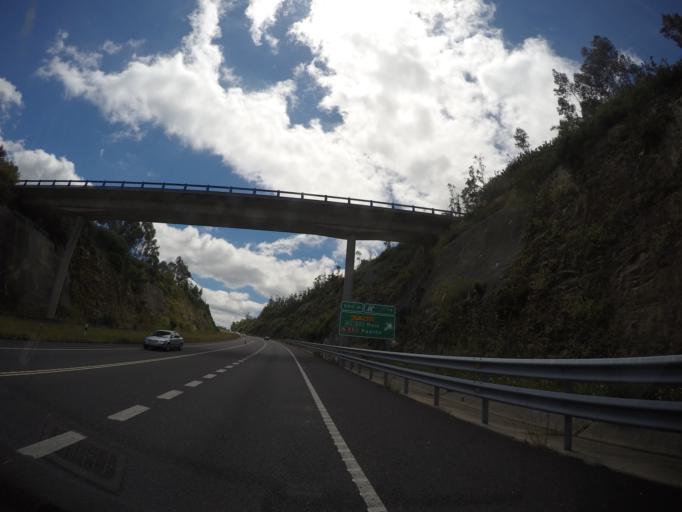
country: ES
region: Aragon
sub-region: Provincia de Zaragoza
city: El Burgo de Ebro
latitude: 41.5520
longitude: -0.7543
